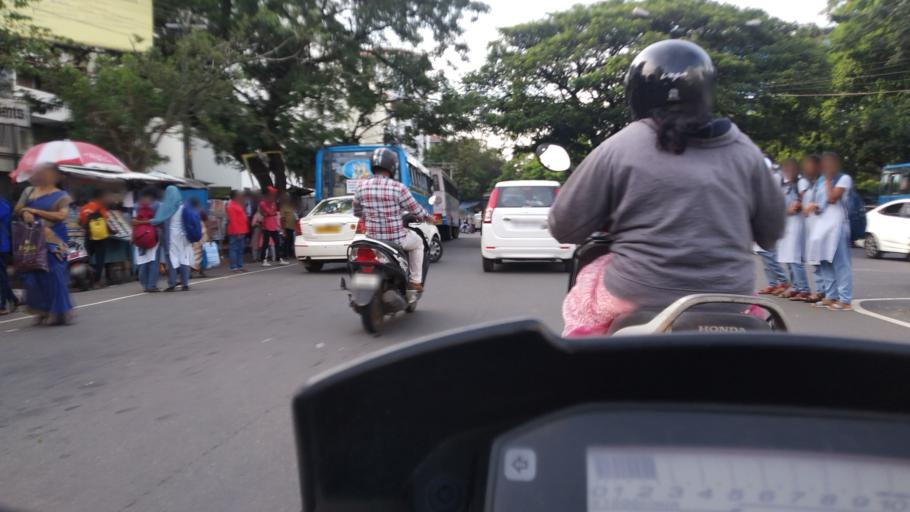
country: IN
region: Kerala
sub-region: Ernakulam
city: Cochin
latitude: 9.9837
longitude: 76.2740
